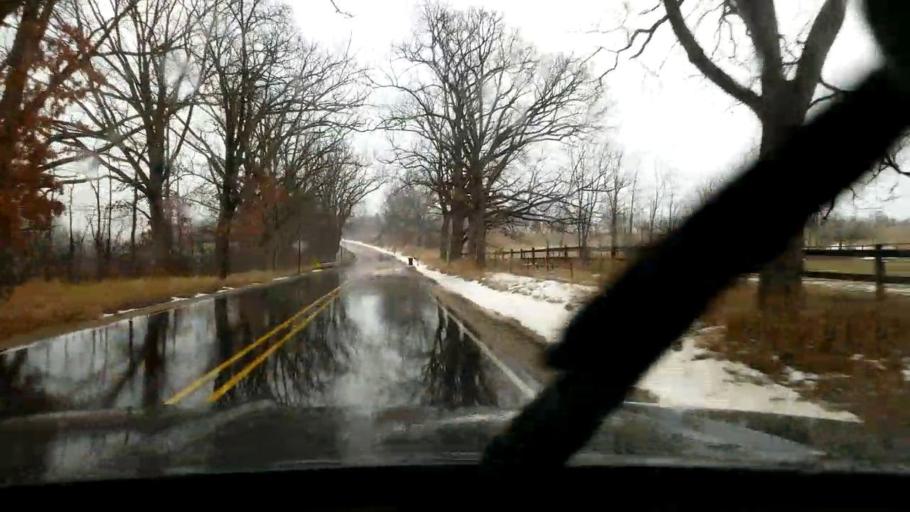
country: US
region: Michigan
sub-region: Jackson County
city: Grass Lake
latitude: 42.3283
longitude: -84.1945
